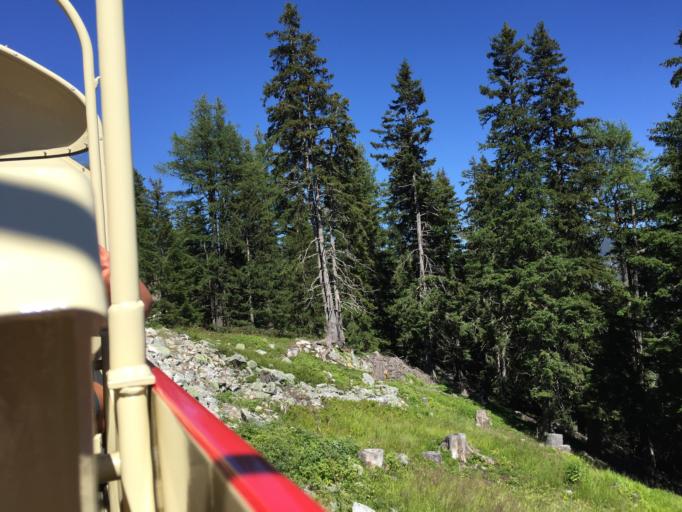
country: CH
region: Valais
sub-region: Saint-Maurice District
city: Salvan
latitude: 46.0639
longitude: 6.9460
